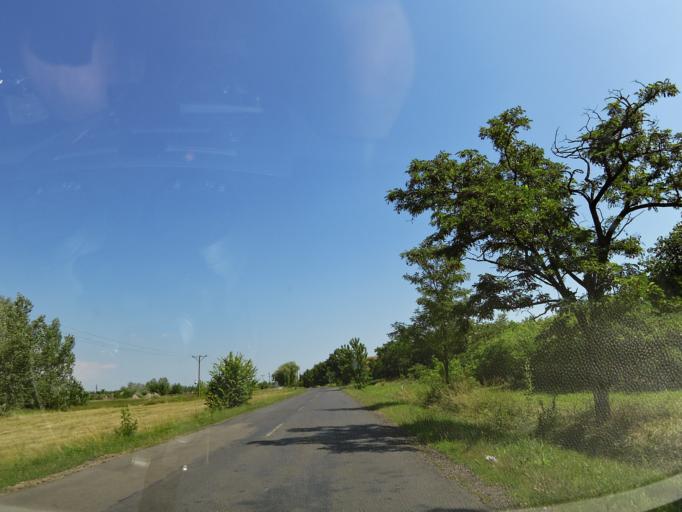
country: HU
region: Jasz-Nagykun-Szolnok
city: Abadszalok
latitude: 47.4667
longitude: 20.5923
